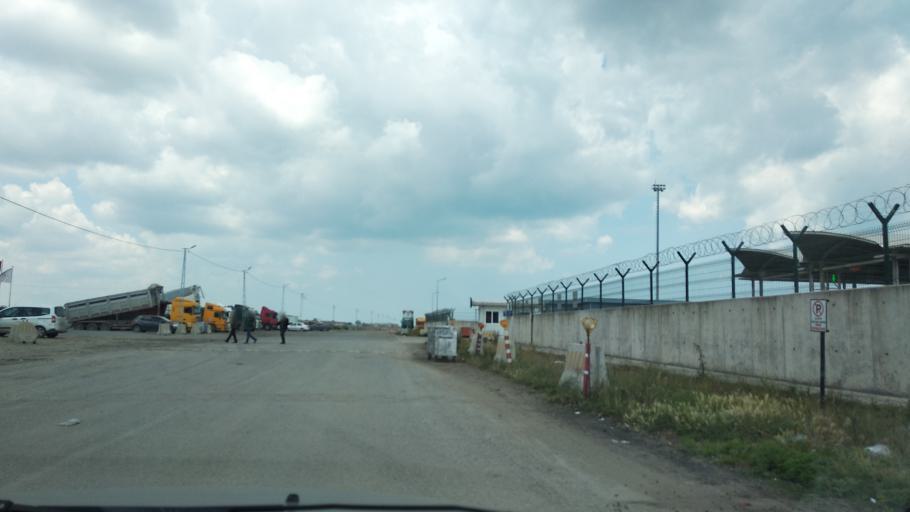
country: TR
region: Sakarya
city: Karasu
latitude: 41.1184
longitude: 30.6705
